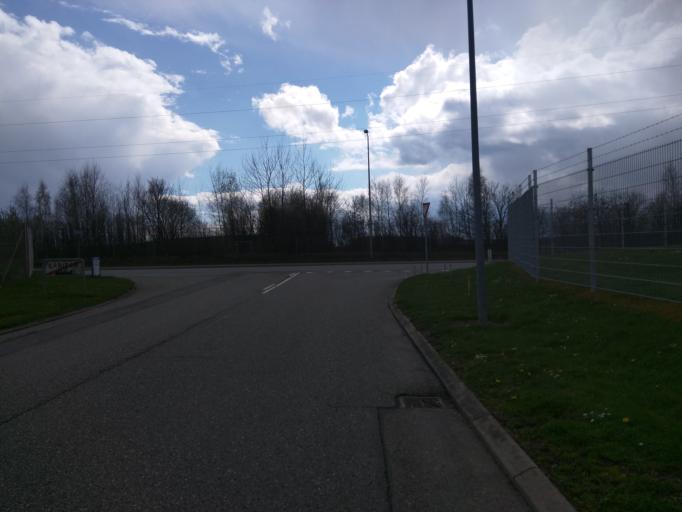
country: DK
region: South Denmark
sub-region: Fredericia Kommune
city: Snoghoj
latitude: 55.5416
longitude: 9.6966
